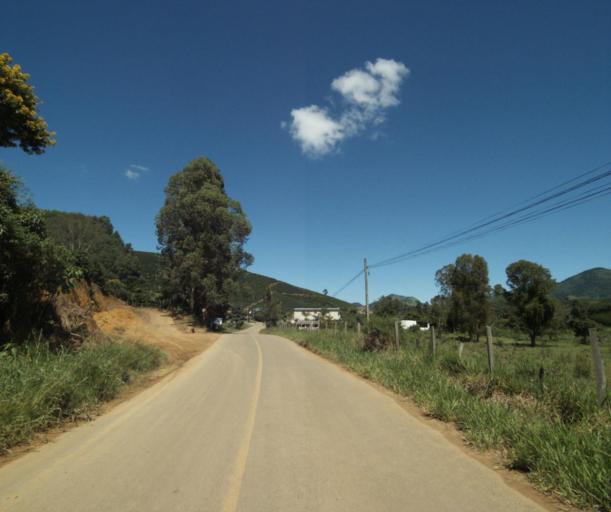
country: BR
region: Minas Gerais
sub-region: Espera Feliz
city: Espera Feliz
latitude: -20.5613
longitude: -41.8235
